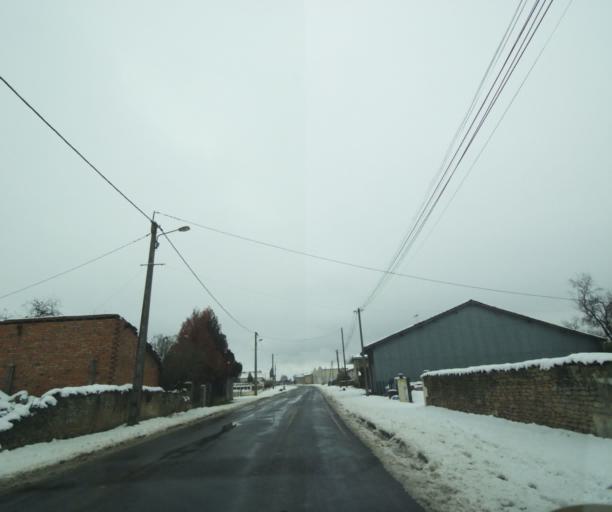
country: FR
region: Champagne-Ardenne
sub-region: Departement de la Haute-Marne
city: Montier-en-Der
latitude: 48.4416
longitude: 4.8034
